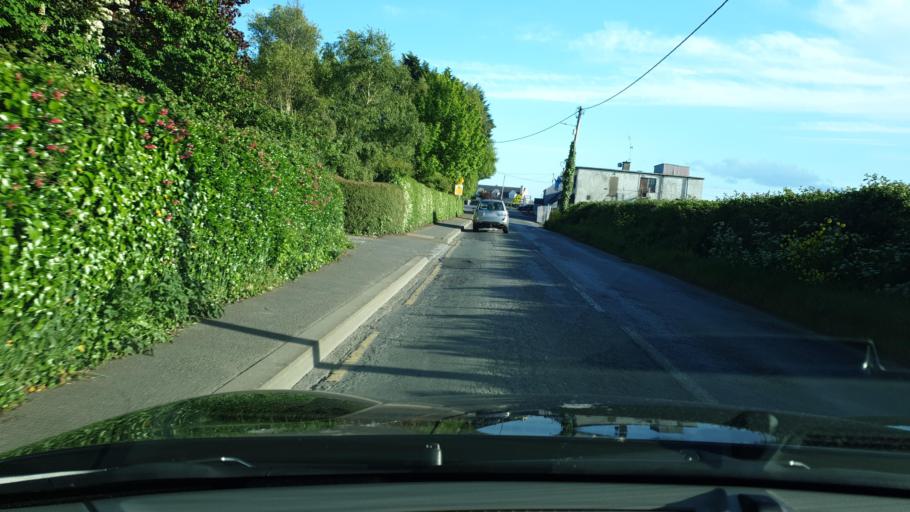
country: IE
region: Leinster
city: An Ros
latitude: 53.5484
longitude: -6.1015
